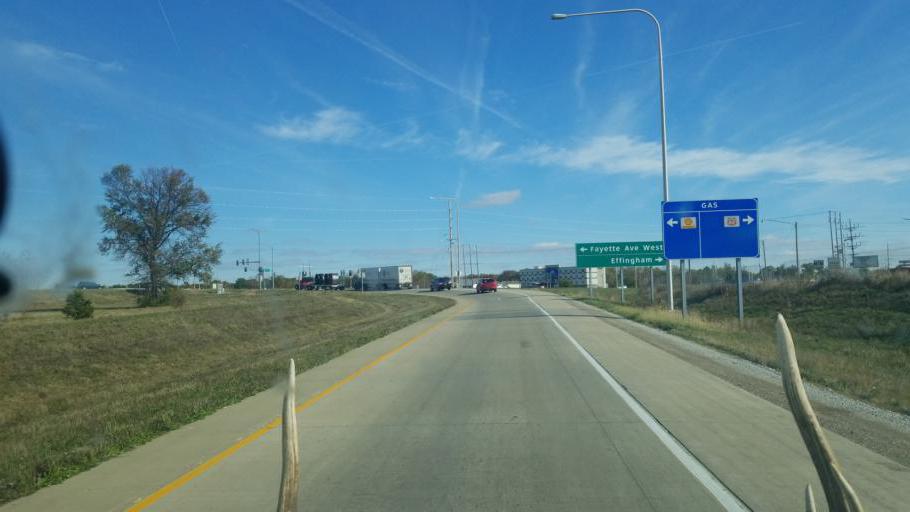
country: US
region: Illinois
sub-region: Effingham County
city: Effingham
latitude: 39.1191
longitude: -88.5681
